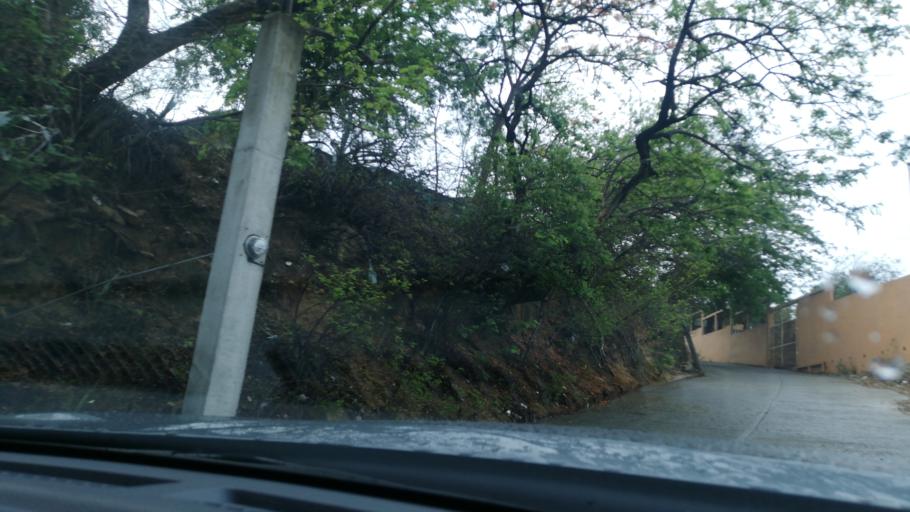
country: MX
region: Oaxaca
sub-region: Salina Cruz
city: Salina Cruz
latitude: 16.1882
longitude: -95.1947
